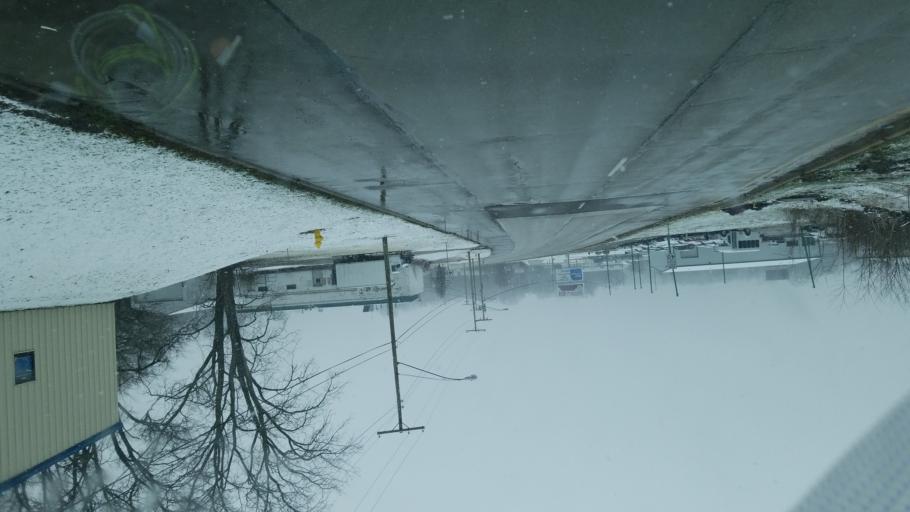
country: US
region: Indiana
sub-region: Grant County
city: Marion
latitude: 40.5578
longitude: -85.6527
